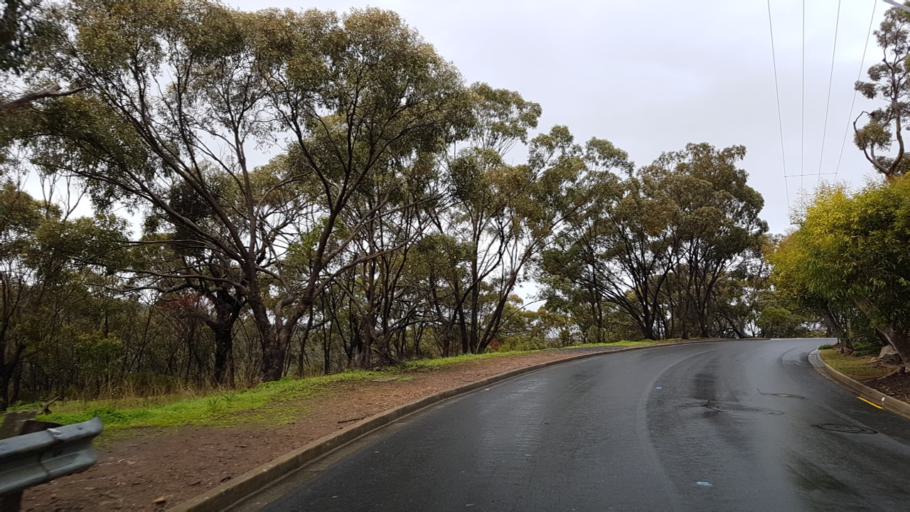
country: AU
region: South Australia
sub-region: Onkaparinga
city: Bedford Park
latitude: -35.0394
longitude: 138.5791
